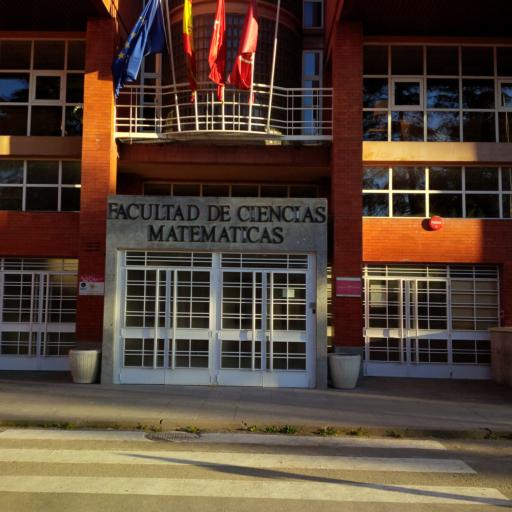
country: ES
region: Madrid
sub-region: Provincia de Madrid
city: Moncloa-Aravaca
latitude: 40.4496
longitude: -3.7259
